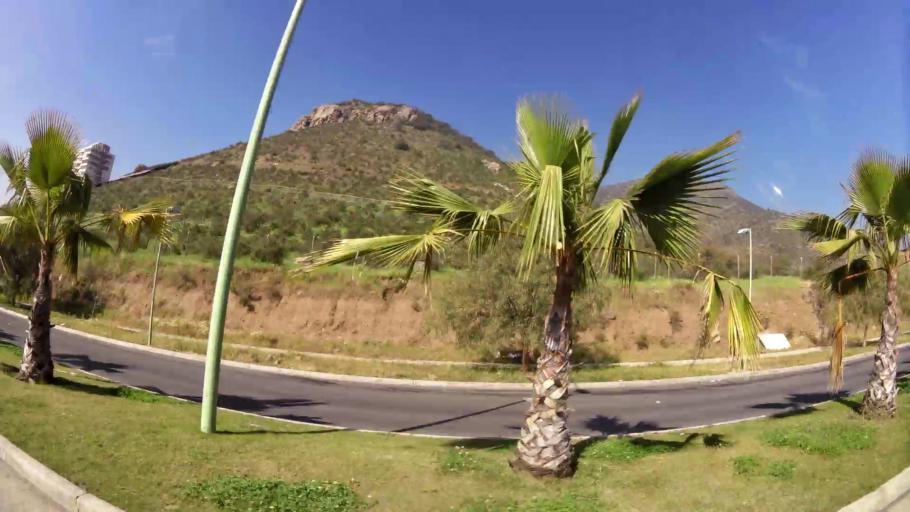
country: CL
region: Santiago Metropolitan
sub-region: Provincia de Santiago
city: Villa Presidente Frei, Nunoa, Santiago, Chile
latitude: -33.4158
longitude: -70.5071
